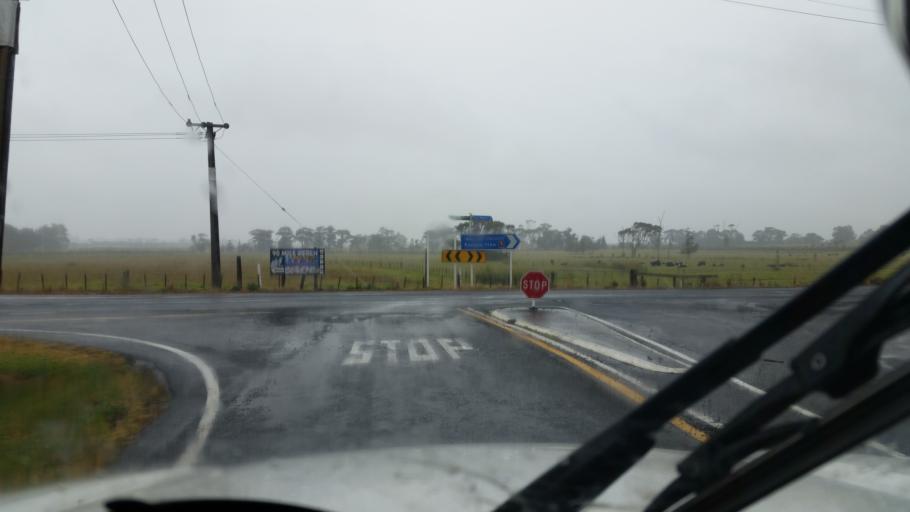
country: NZ
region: Northland
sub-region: Far North District
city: Ahipara
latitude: -35.1723
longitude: 173.1801
